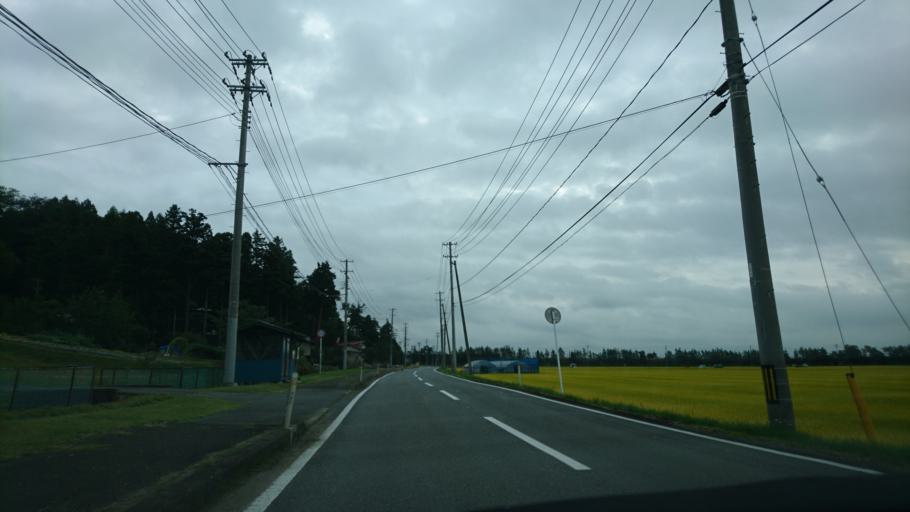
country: JP
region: Iwate
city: Ichinoseki
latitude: 38.8045
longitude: 141.0894
